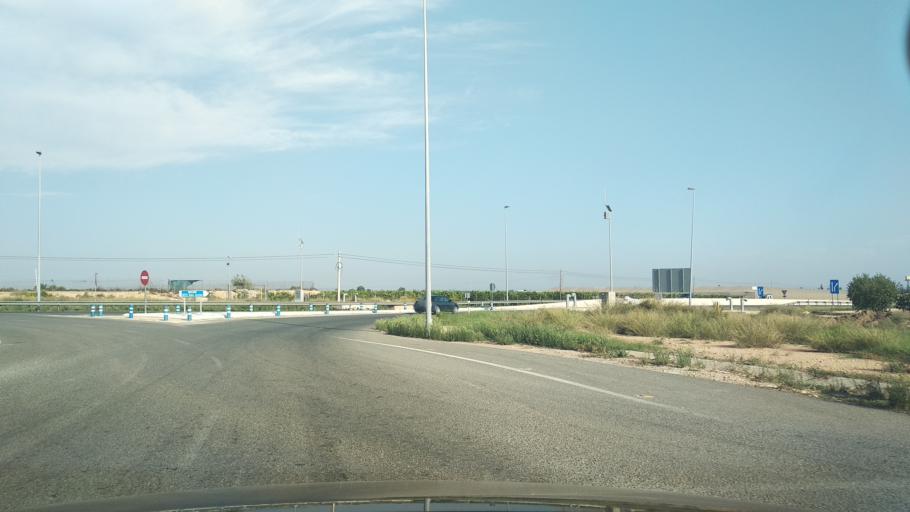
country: ES
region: Murcia
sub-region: Murcia
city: San Javier
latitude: 37.8208
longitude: -0.8493
